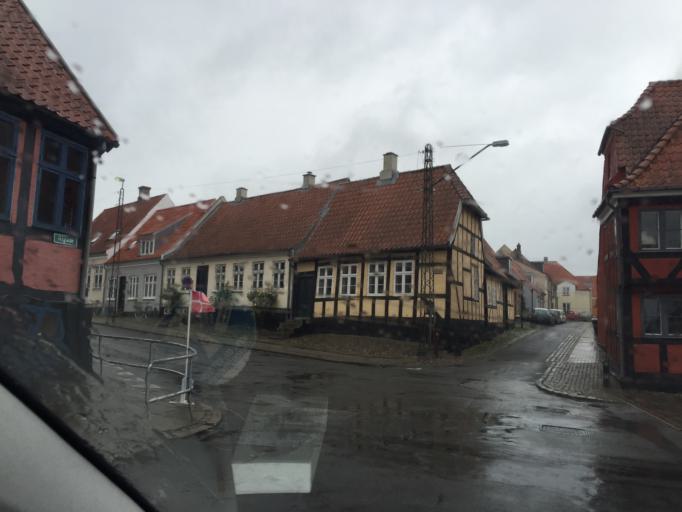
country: DK
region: South Denmark
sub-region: Middelfart Kommune
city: Middelfart
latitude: 55.5065
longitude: 9.7273
